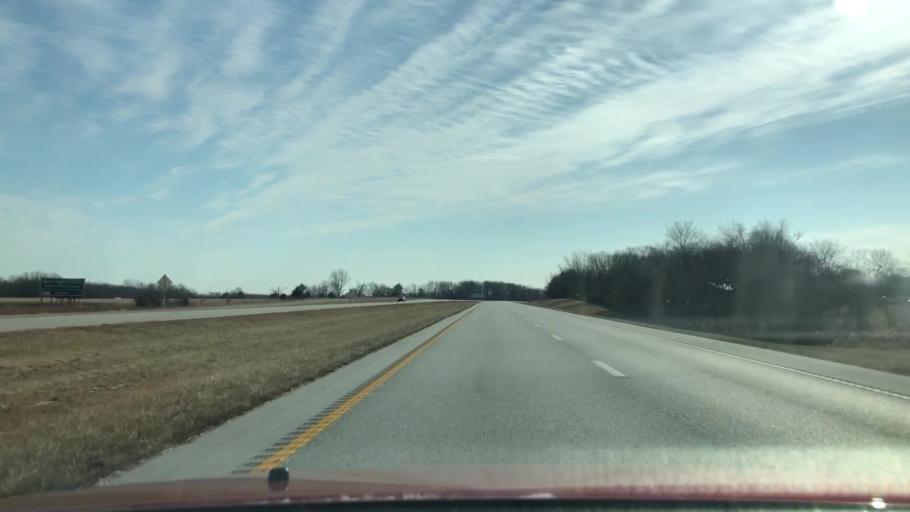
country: US
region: Missouri
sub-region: Webster County
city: Seymour
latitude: 37.1480
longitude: -92.7515
